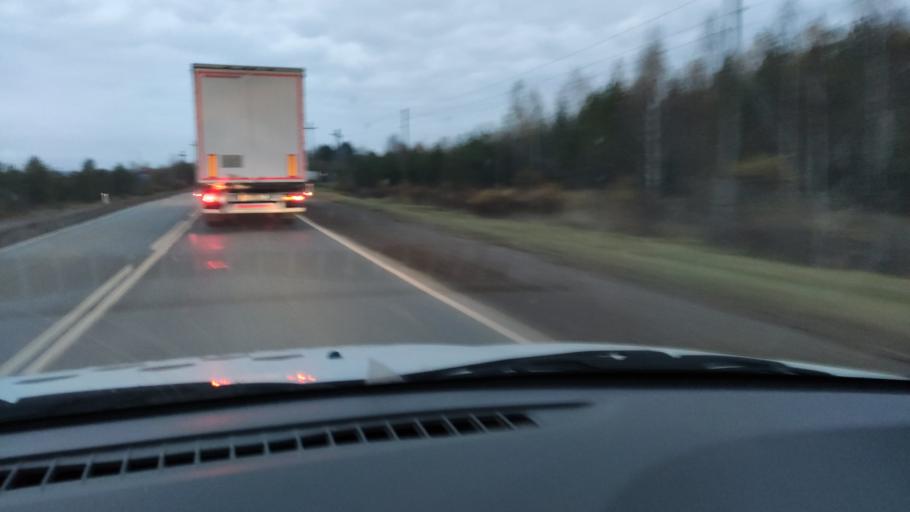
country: RU
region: Kirov
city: Kostino
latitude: 58.8545
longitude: 53.2086
